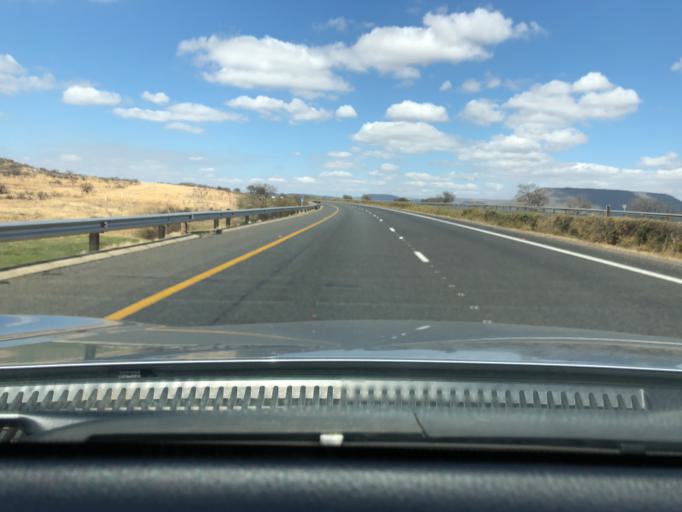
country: ZA
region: KwaZulu-Natal
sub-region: uThukela District Municipality
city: Ladysmith
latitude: -28.6786
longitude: 29.6338
